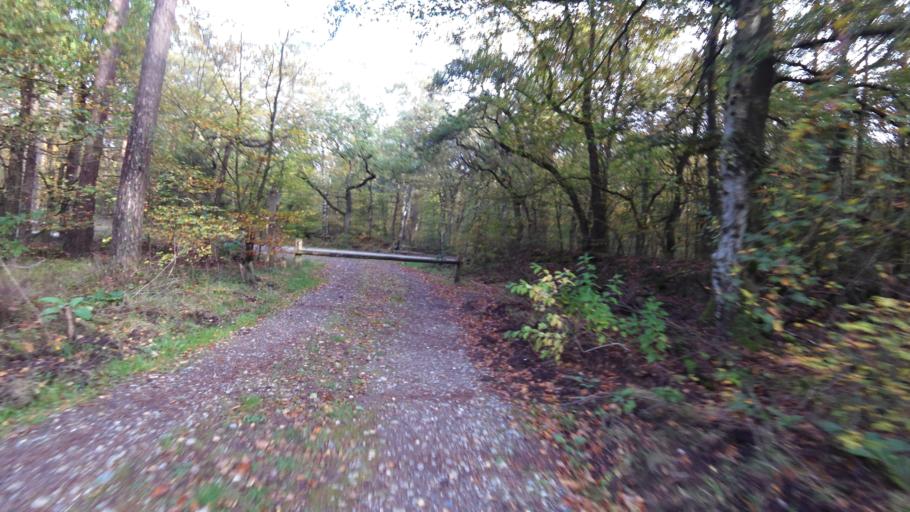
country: NL
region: Gelderland
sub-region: Gemeente Epe
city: Epe
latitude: 52.3556
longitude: 5.9107
